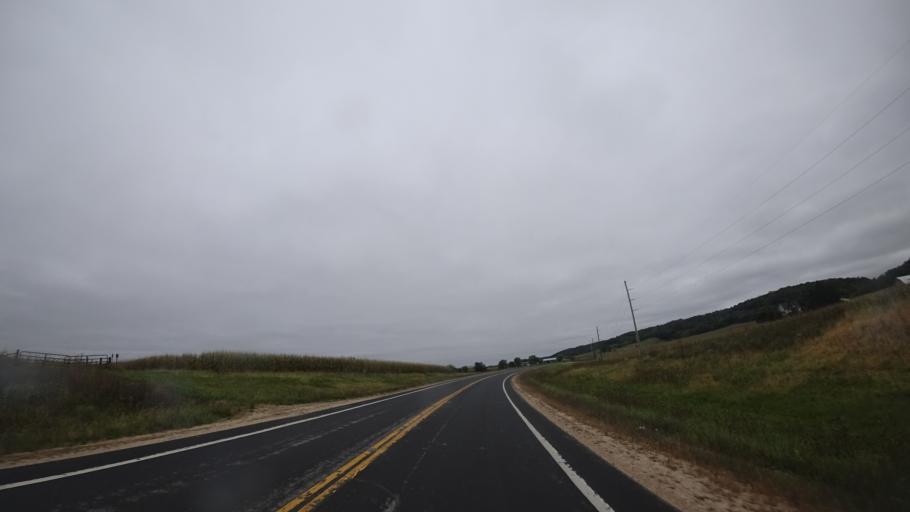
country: US
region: Wisconsin
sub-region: Grant County
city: Boscobel
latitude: 43.1052
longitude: -90.8121
